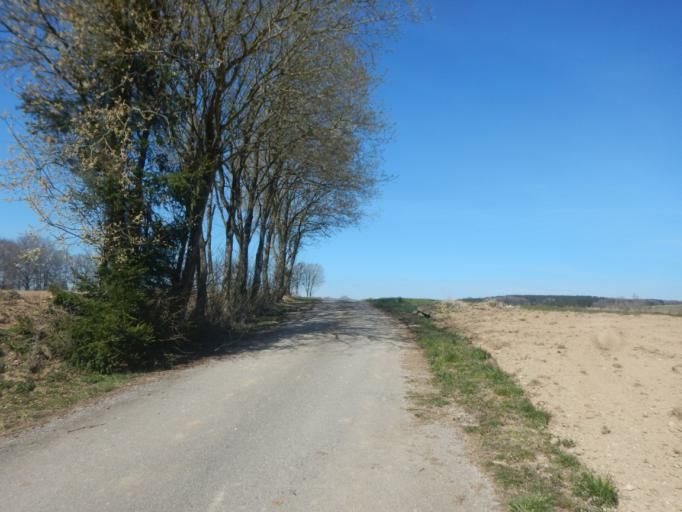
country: LU
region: Diekirch
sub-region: Canton de Clervaux
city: Weiswampach
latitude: 50.1175
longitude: 6.0483
